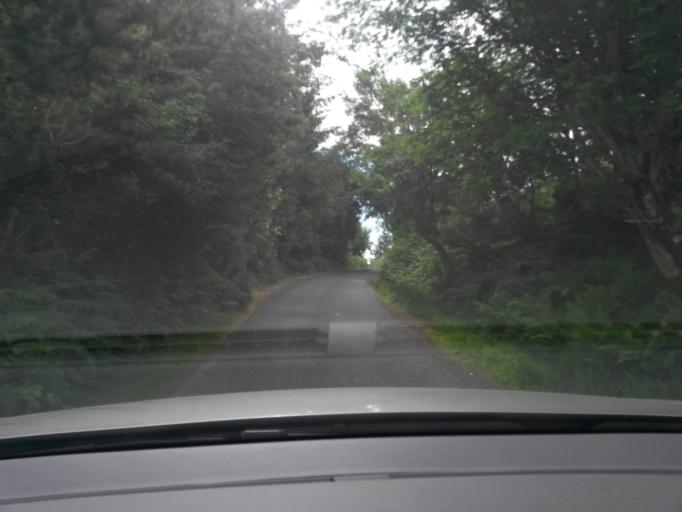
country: IE
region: Leinster
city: Ballinteer
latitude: 53.1811
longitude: -6.2697
